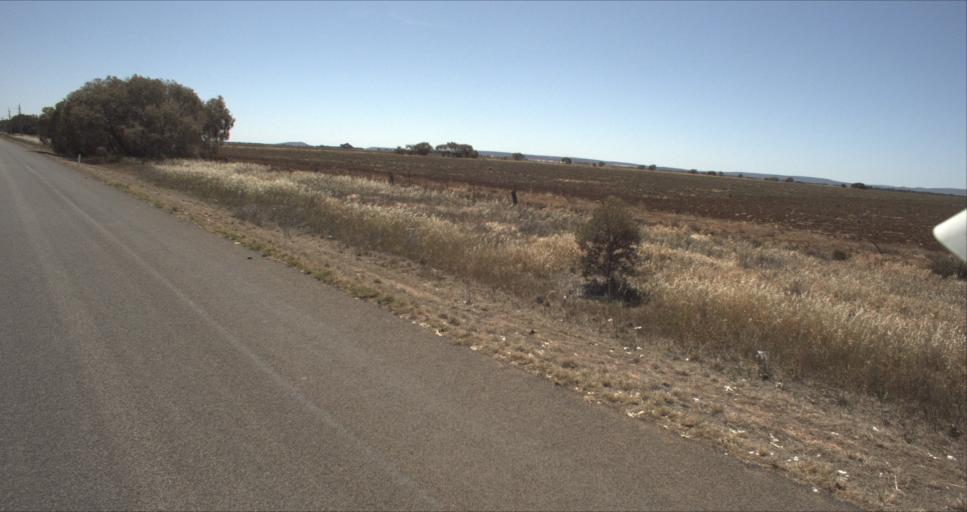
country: AU
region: New South Wales
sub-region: Leeton
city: Leeton
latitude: -34.4764
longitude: 146.2914
